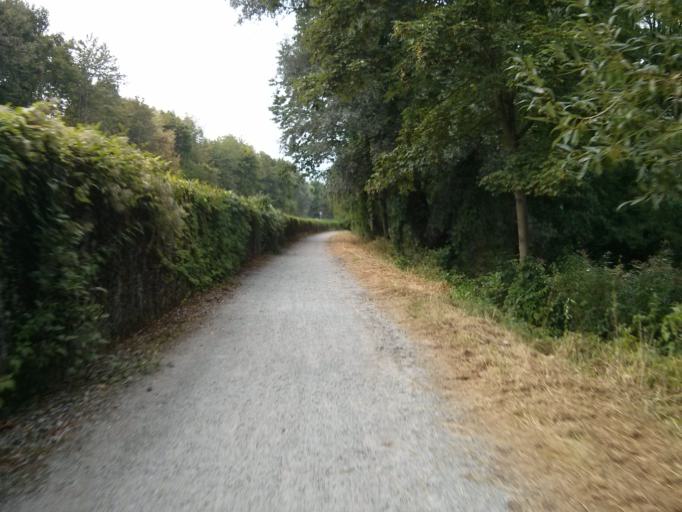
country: DE
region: Bavaria
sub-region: Lower Bavaria
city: Deggendorf
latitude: 48.8461
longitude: 12.9550
